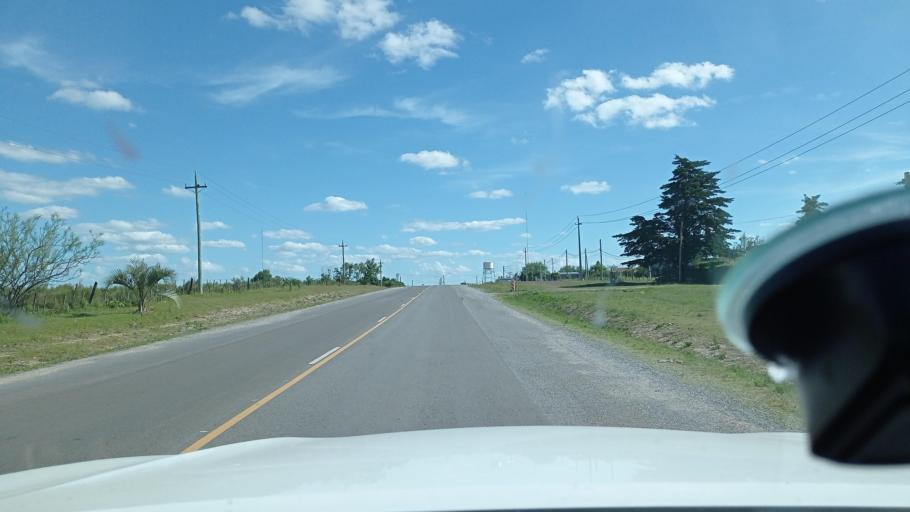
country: UY
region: Florida
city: Florida
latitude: -34.0829
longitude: -56.2363
